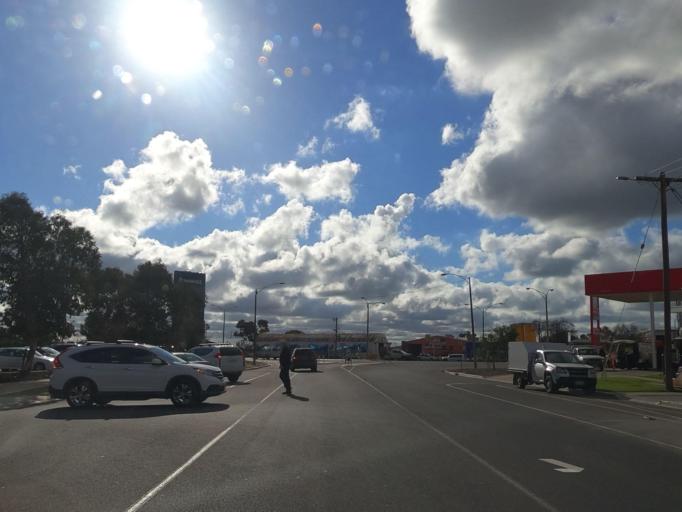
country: AU
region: Victoria
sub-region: Swan Hill
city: Swan Hill
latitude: -35.3347
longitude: 143.5568
